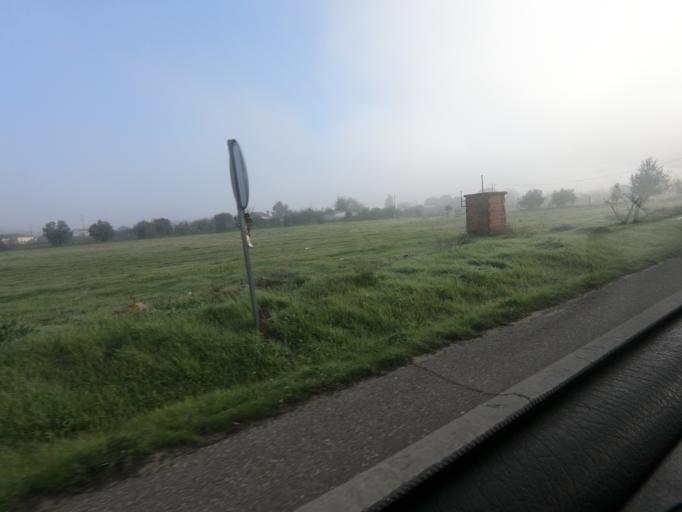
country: PT
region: Setubal
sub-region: Palmela
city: Pinhal Novo
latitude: 38.6043
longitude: -8.9053
